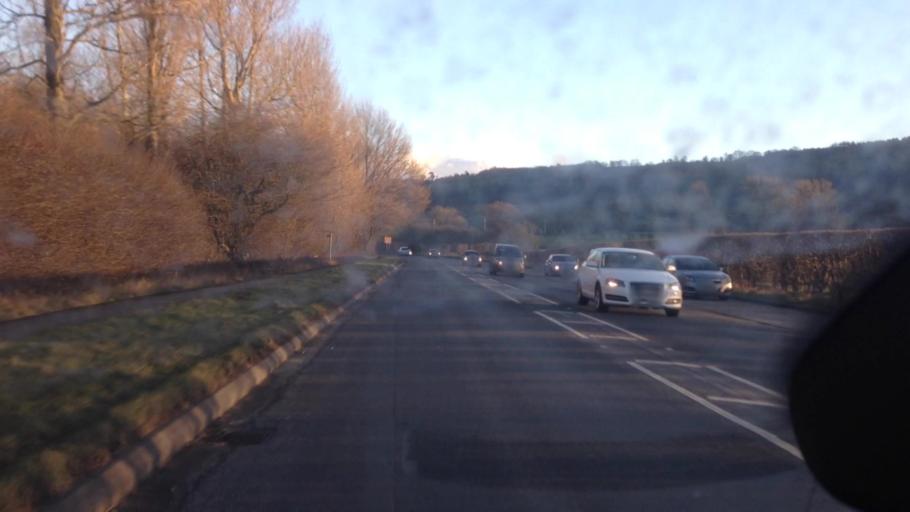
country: GB
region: England
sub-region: City and Borough of Leeds
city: Otley
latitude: 53.9074
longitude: -1.6584
